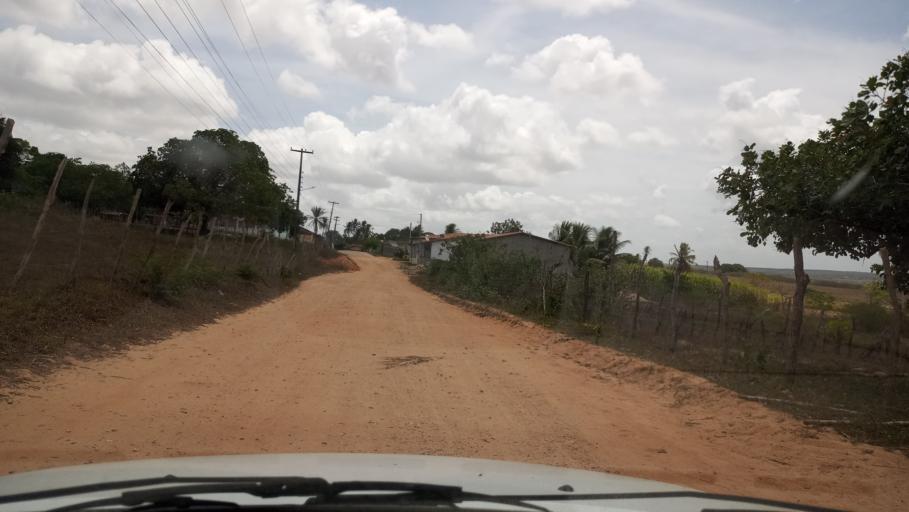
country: BR
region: Rio Grande do Norte
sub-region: Goianinha
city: Goianinha
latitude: -6.2902
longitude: -35.2835
